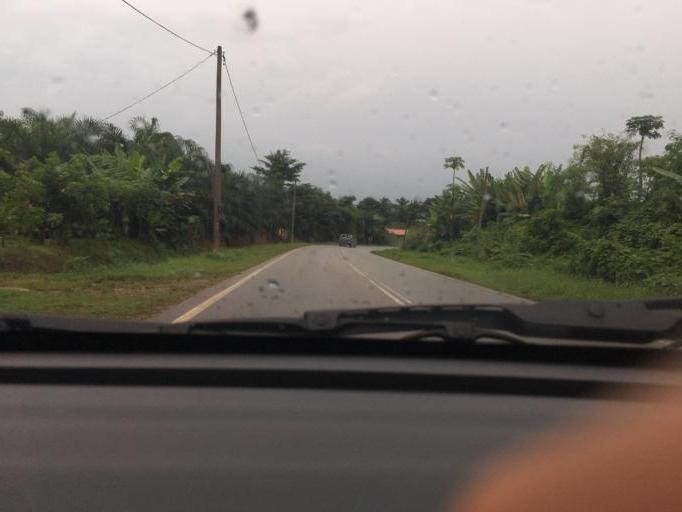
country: MY
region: Kedah
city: Bedong
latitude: 5.6975
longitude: 100.6331
